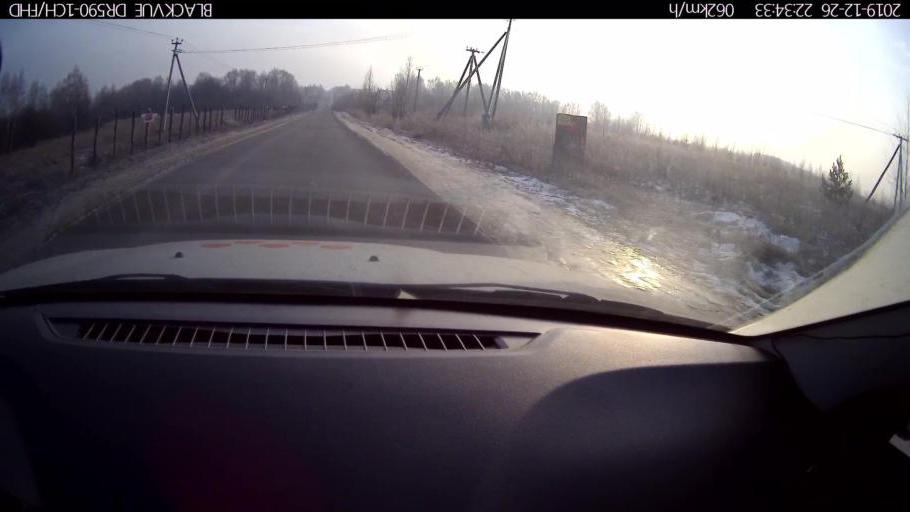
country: RU
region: Nizjnij Novgorod
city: Burevestnik
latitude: 56.1554
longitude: 43.7105
